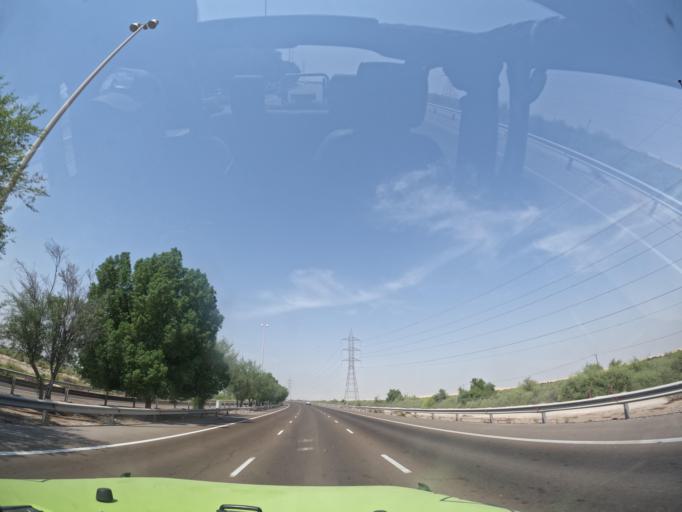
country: AE
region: Abu Dhabi
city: Abu Dhabi
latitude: 24.2146
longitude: 54.8843
